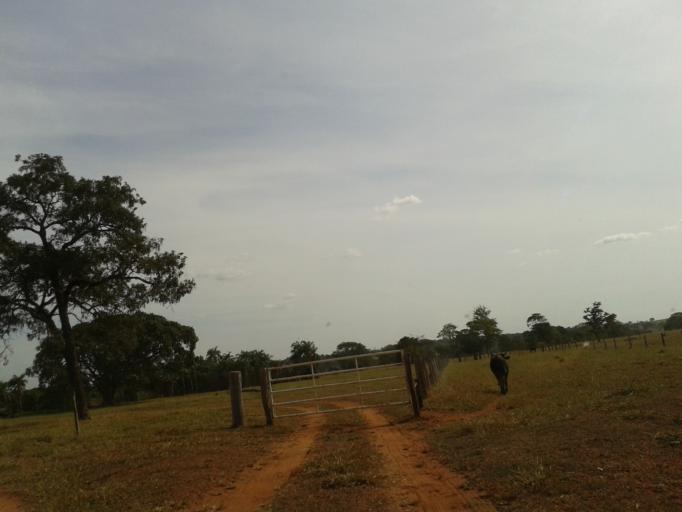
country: BR
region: Minas Gerais
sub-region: Campina Verde
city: Campina Verde
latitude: -19.5142
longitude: -49.5954
